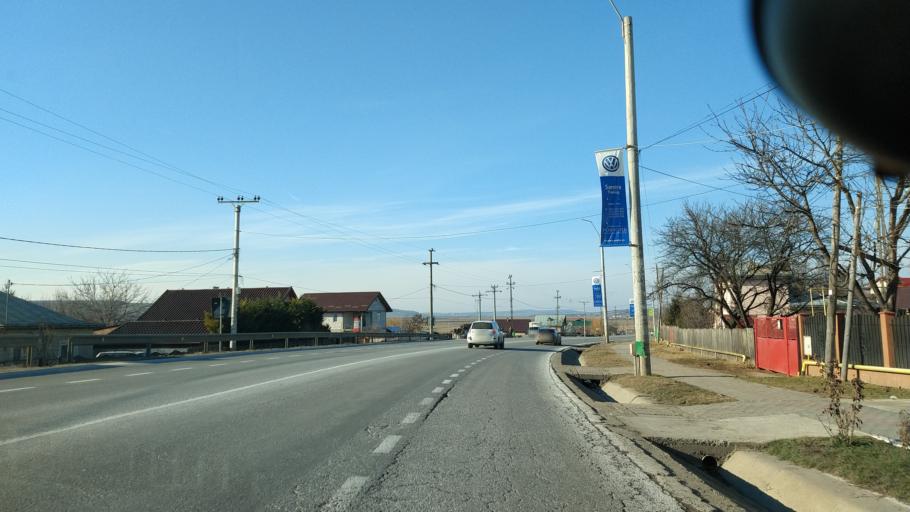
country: RO
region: Iasi
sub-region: Comuna Letcani
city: Letcani
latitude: 47.1958
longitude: 27.3992
